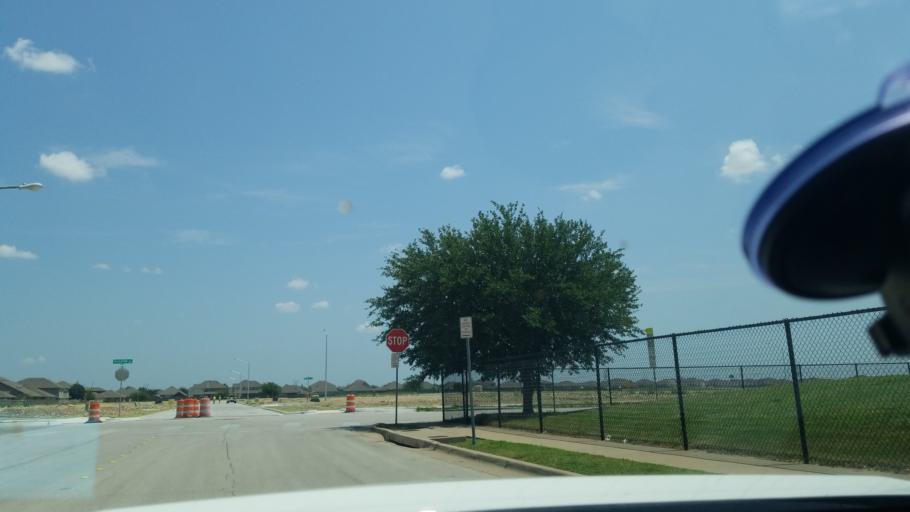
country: US
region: Texas
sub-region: Tarrant County
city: Saginaw
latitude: 32.9177
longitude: -97.3722
